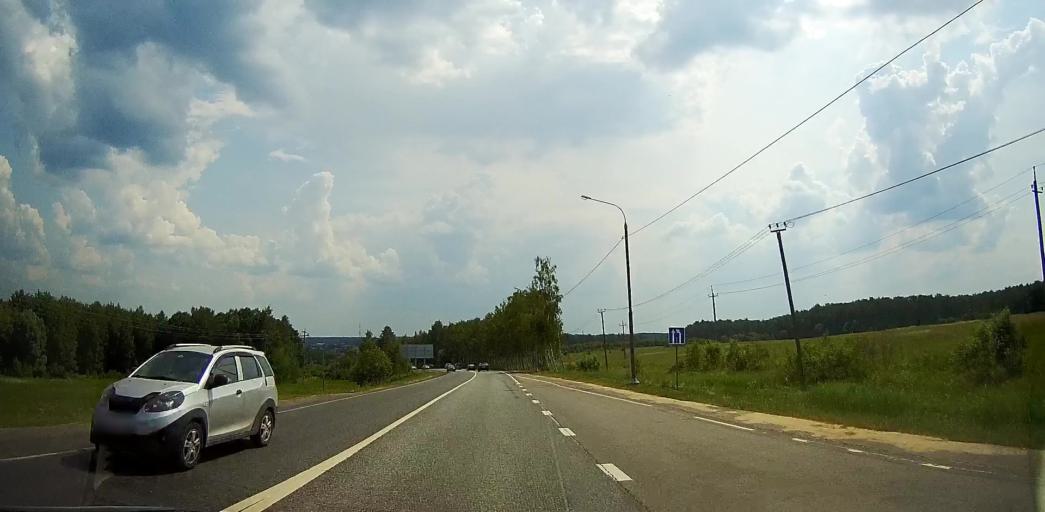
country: RU
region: Moskovskaya
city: Stupino
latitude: 54.9539
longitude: 38.1255
